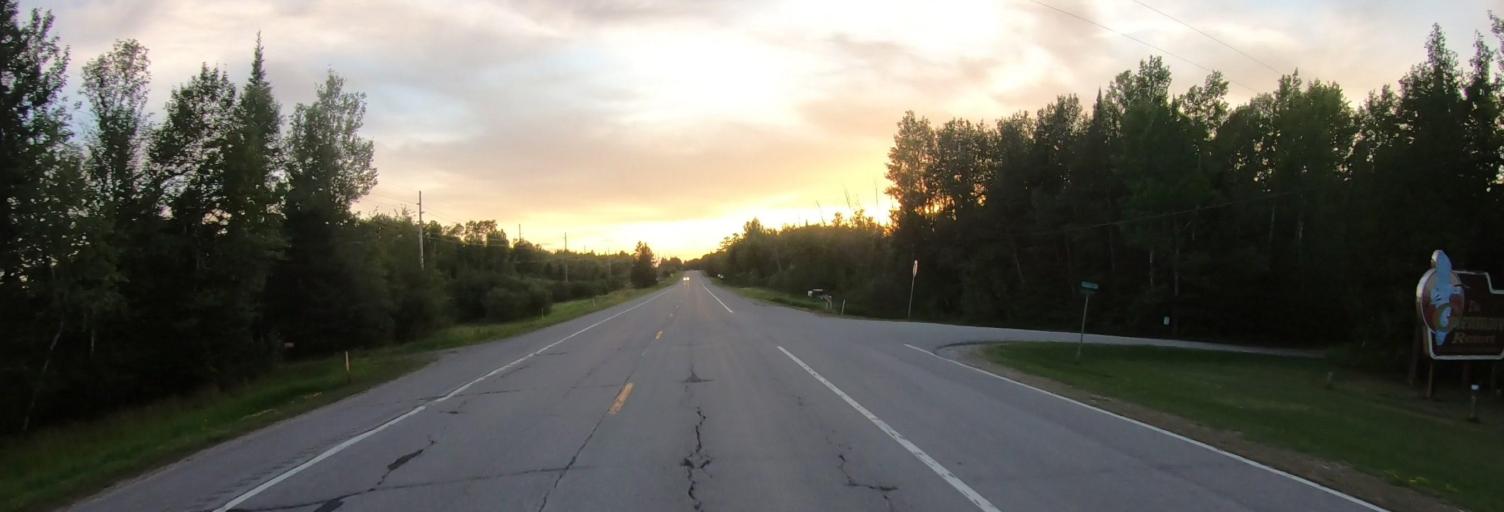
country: US
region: Minnesota
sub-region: Saint Louis County
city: Aurora
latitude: 47.7971
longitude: -92.3192
